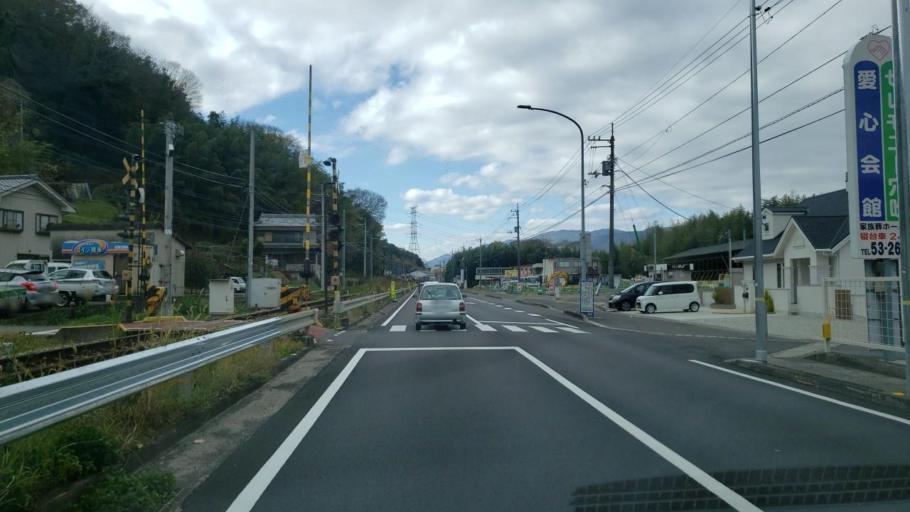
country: JP
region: Tokushima
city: Wakimachi
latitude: 34.0549
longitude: 134.1379
